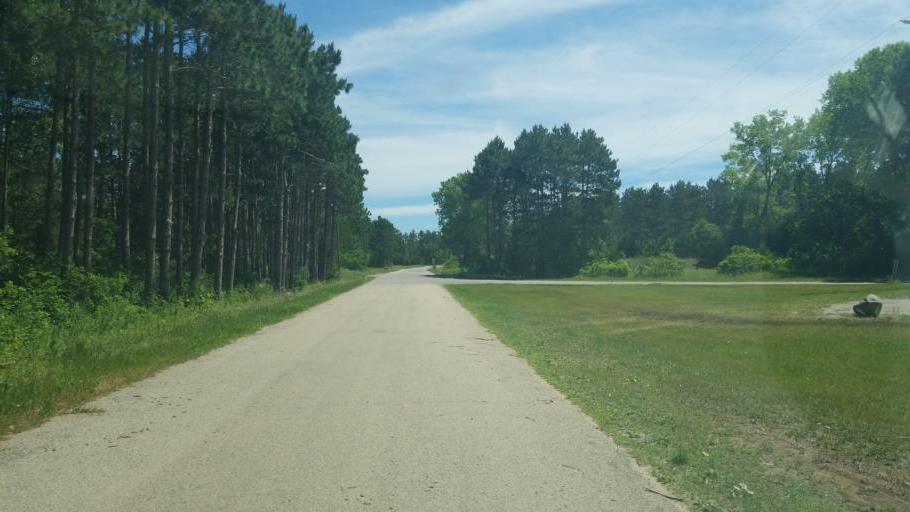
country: US
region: Wisconsin
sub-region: Juneau County
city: Mauston
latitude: 43.8663
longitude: -89.9527
